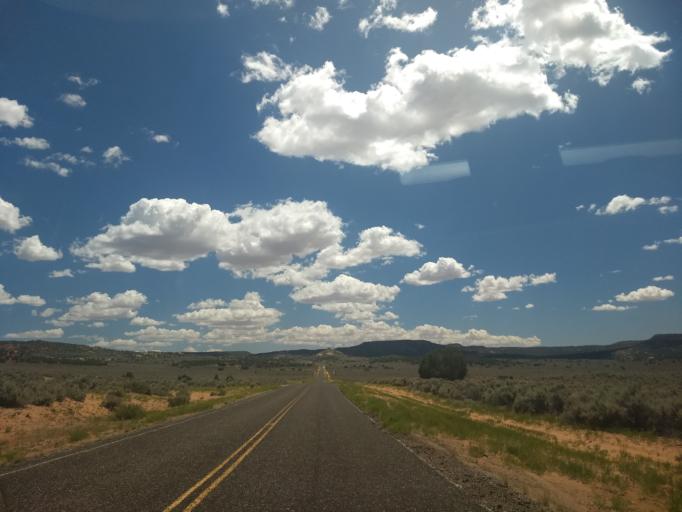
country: US
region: Utah
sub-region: Kane County
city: Kanab
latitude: 37.1657
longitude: -112.6646
